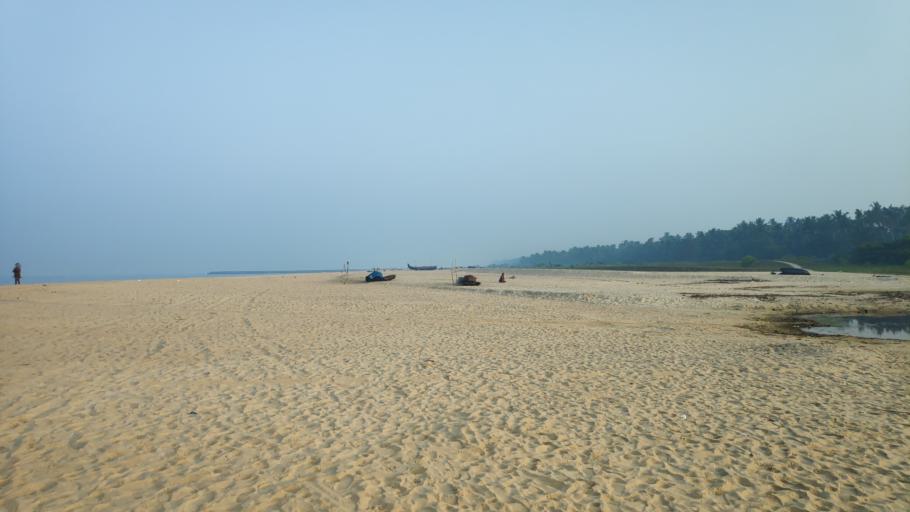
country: IN
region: Kerala
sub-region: Alappuzha
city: Vayalar
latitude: 9.6622
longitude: 76.2917
